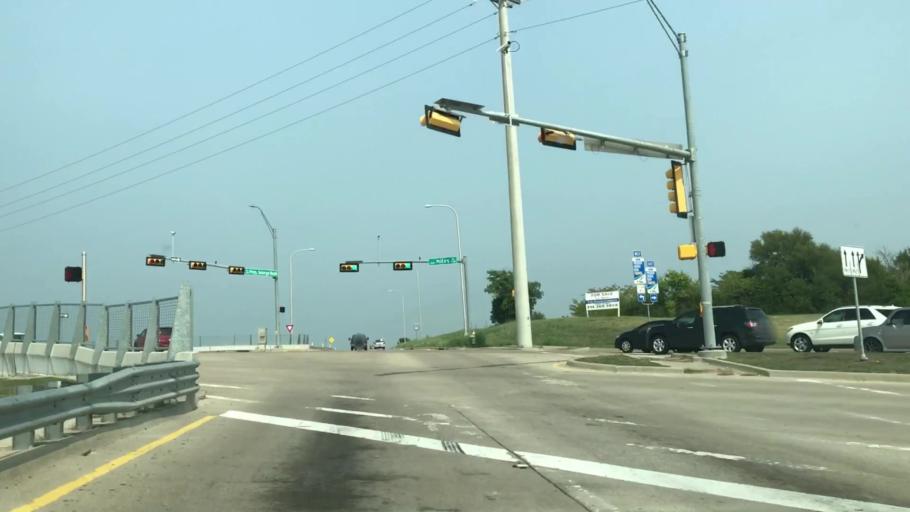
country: US
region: Texas
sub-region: Dallas County
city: Sachse
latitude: 32.9503
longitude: -96.5849
